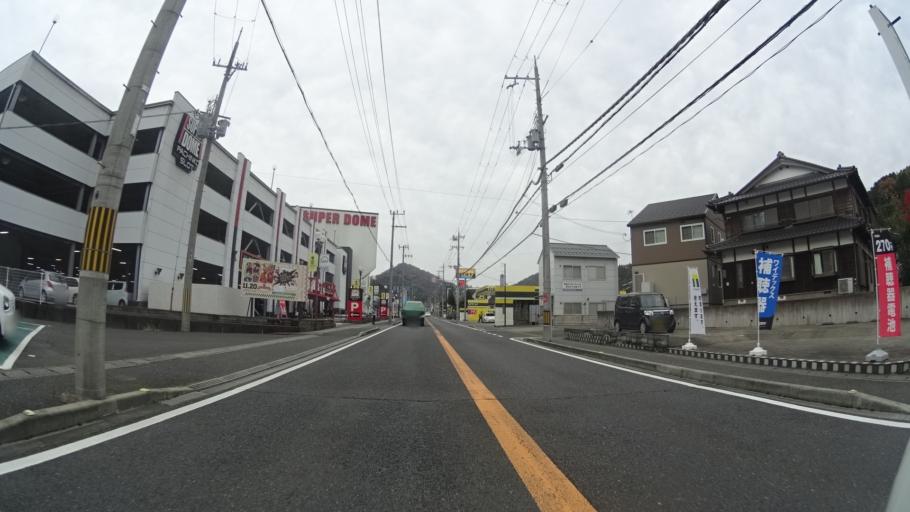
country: JP
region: Kyoto
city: Maizuru
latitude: 35.4485
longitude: 135.3515
